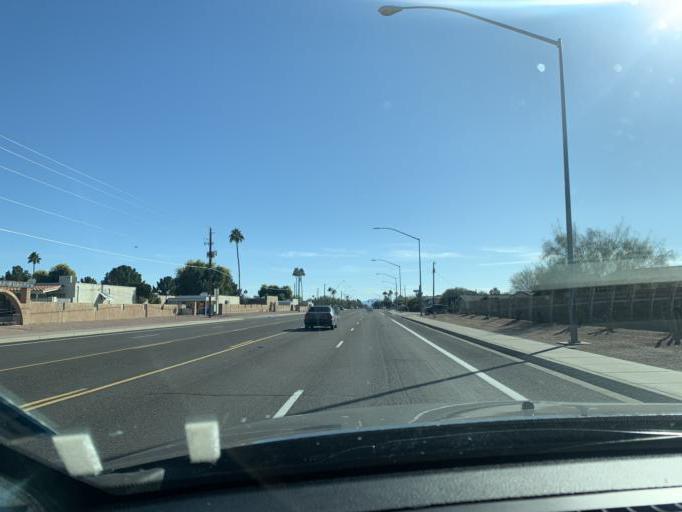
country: US
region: Arizona
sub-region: Maricopa County
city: Mesa
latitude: 33.4556
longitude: -111.7015
